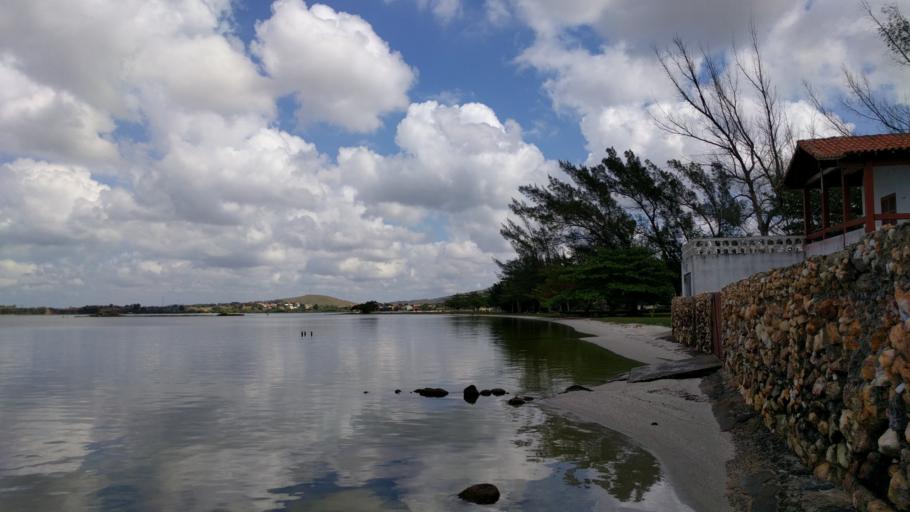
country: BR
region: Rio de Janeiro
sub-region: Sao Pedro Da Aldeia
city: Sao Pedro da Aldeia
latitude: -22.8428
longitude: -42.1269
